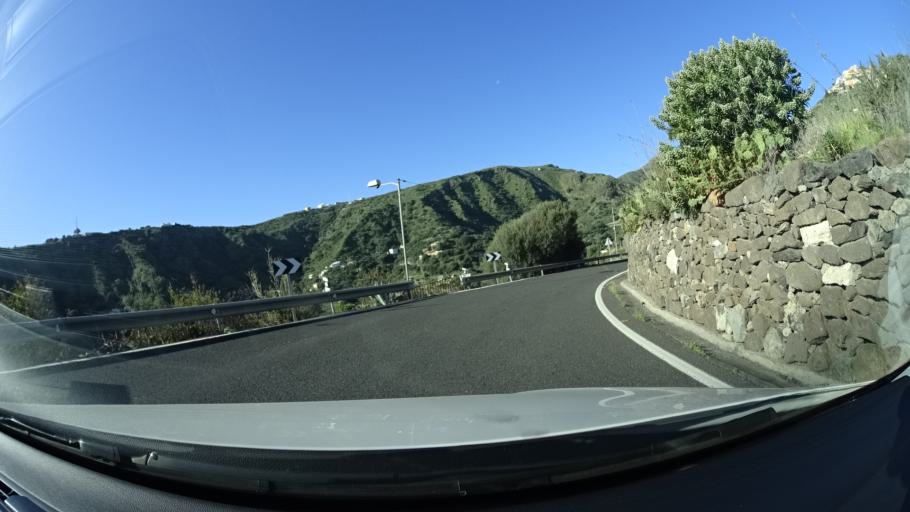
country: ES
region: Canary Islands
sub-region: Provincia de Las Palmas
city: Santa Brigida
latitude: 28.0242
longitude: -15.4712
